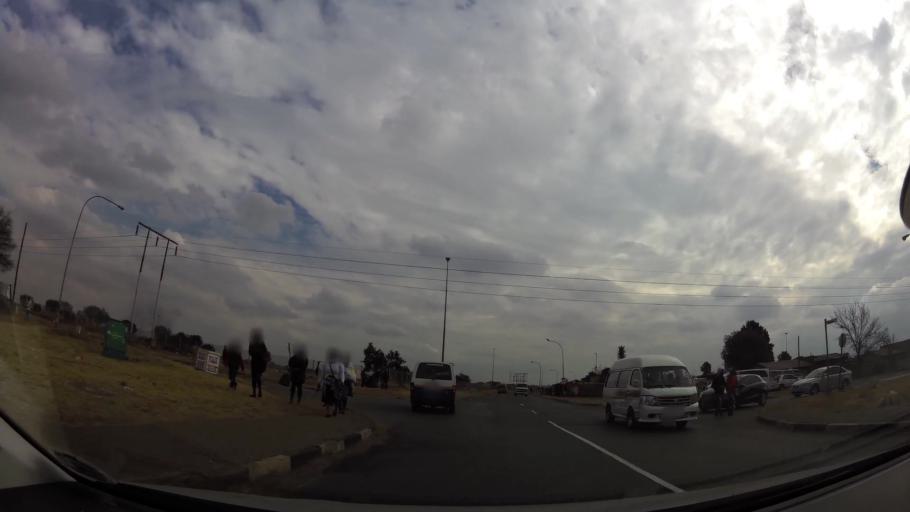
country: ZA
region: Gauteng
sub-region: City of Johannesburg Metropolitan Municipality
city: Soweto
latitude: -26.2728
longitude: 27.8608
